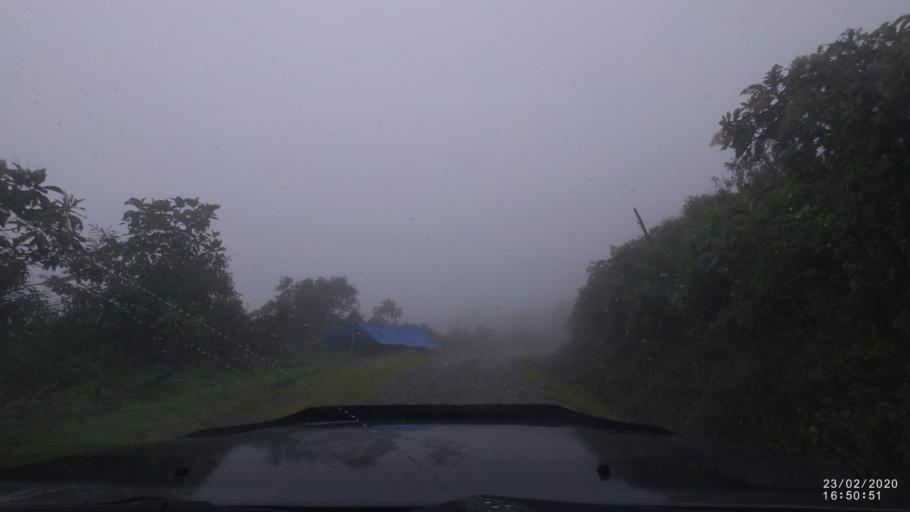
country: BO
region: Cochabamba
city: Colomi
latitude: -17.0915
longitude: -65.9843
